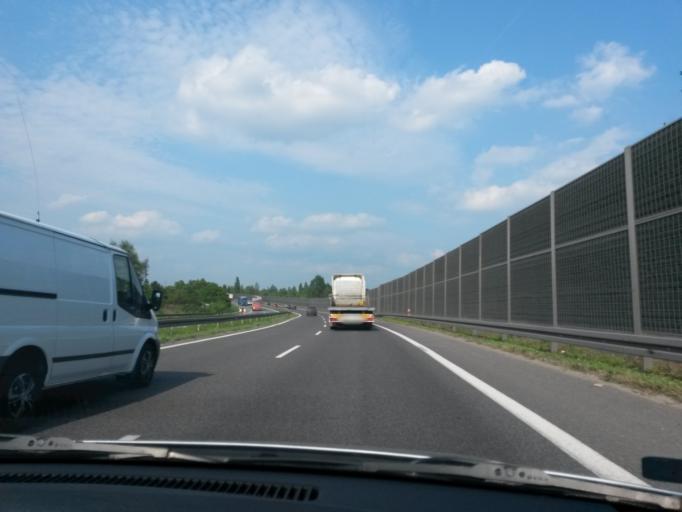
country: PL
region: Silesian Voivodeship
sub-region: Dabrowa Gornicza
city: Dabrowa Gornicza
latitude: 50.2695
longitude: 19.2017
